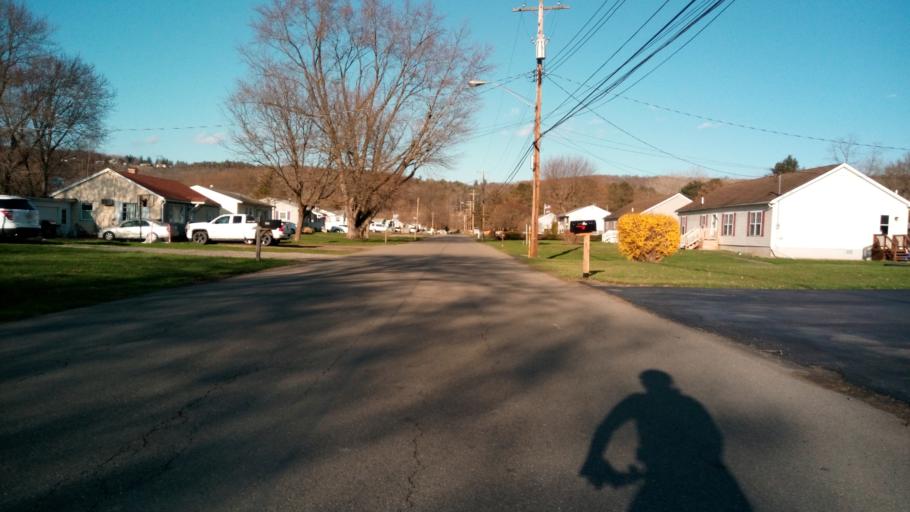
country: US
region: New York
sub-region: Chemung County
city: Elmira
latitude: 42.0757
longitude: -76.7828
